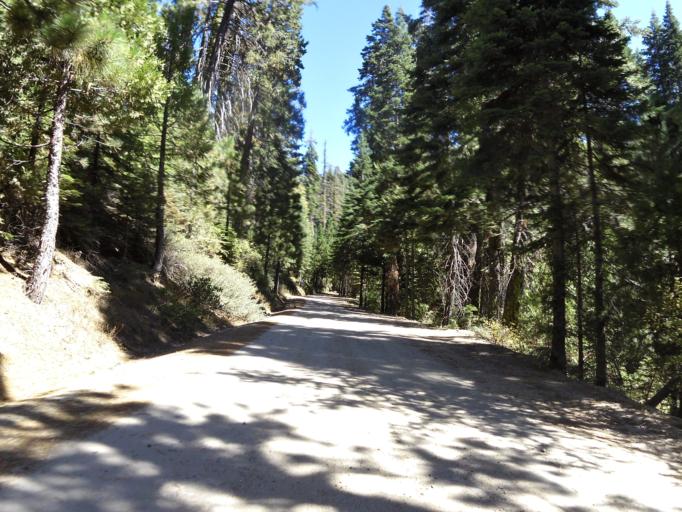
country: US
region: California
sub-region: Madera County
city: Oakhurst
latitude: 37.4452
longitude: -119.5215
